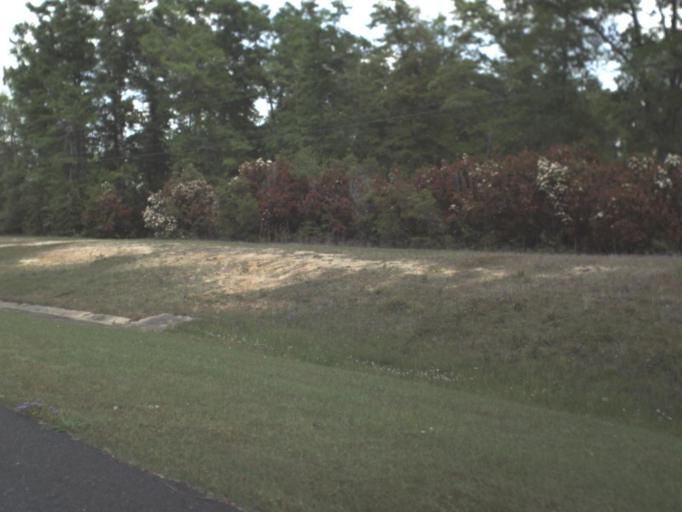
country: US
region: Florida
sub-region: Escambia County
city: Molino
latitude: 30.8195
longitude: -87.3343
